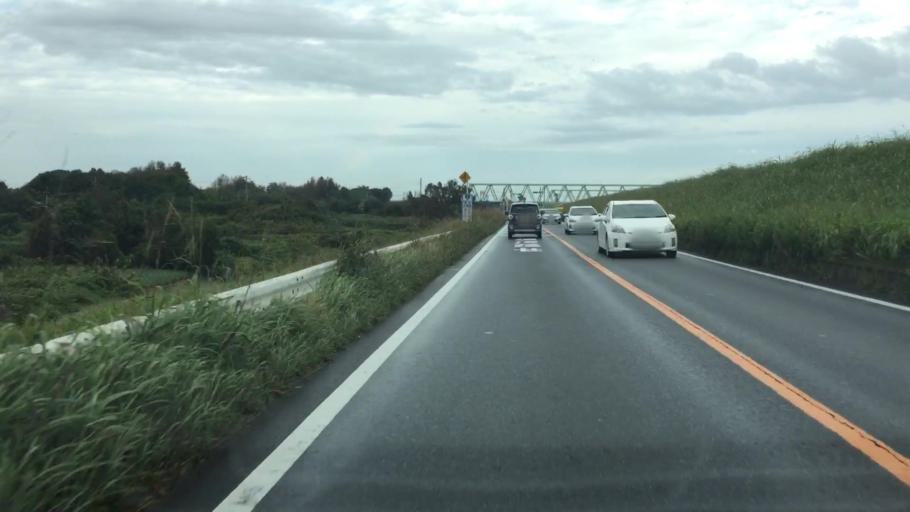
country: JP
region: Ibaraki
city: Toride
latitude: 35.8831
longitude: 140.0619
